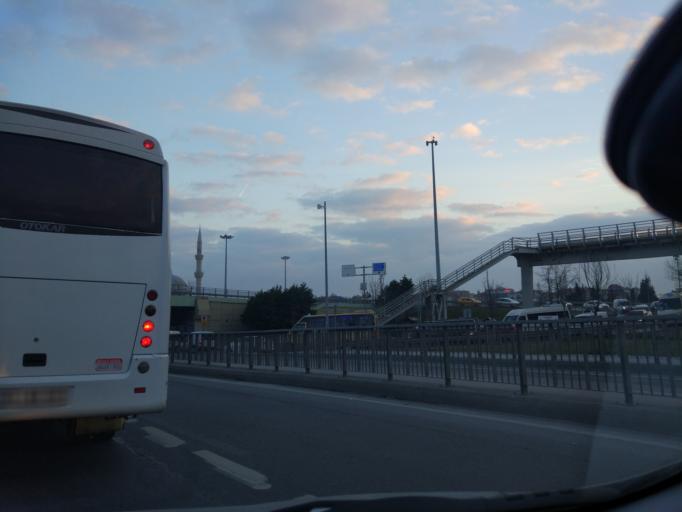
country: TR
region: Istanbul
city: Yakuplu
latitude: 40.9860
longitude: 28.7215
